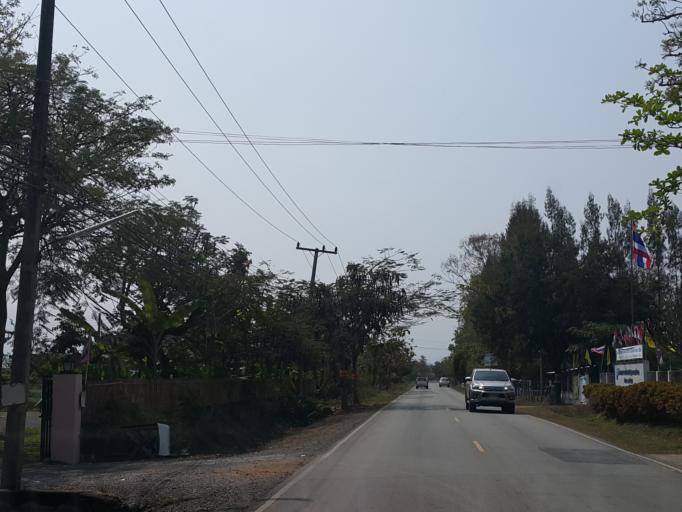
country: TH
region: Chiang Mai
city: San Kamphaeng
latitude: 18.6979
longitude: 99.1035
